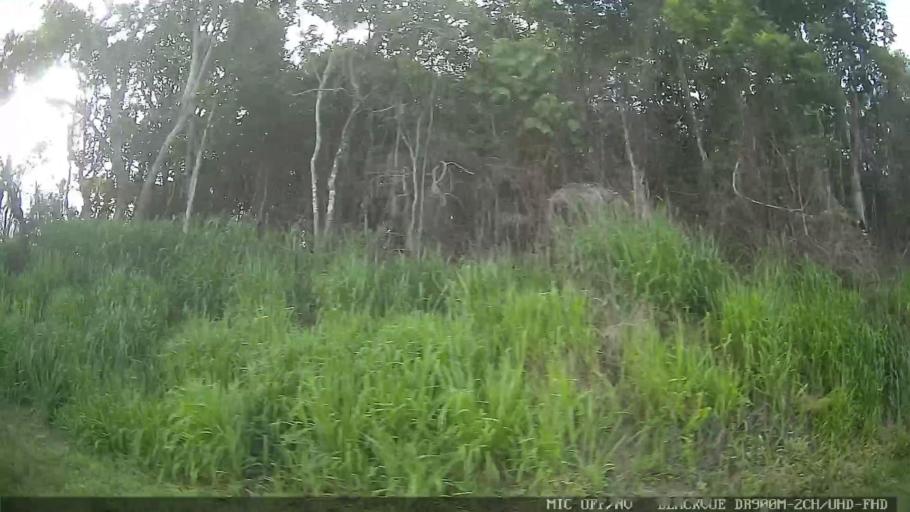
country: BR
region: Sao Paulo
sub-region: Mogi das Cruzes
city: Mogi das Cruzes
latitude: -23.5385
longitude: -46.1574
